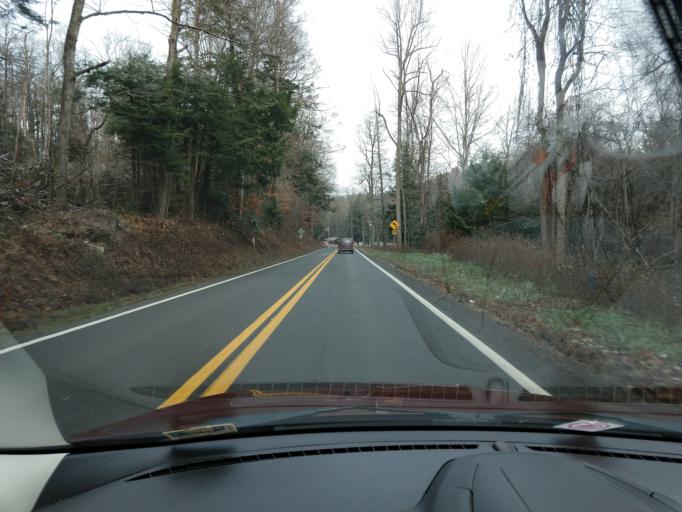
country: US
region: West Virginia
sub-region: Nicholas County
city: Craigsville
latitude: 38.2575
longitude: -80.7285
